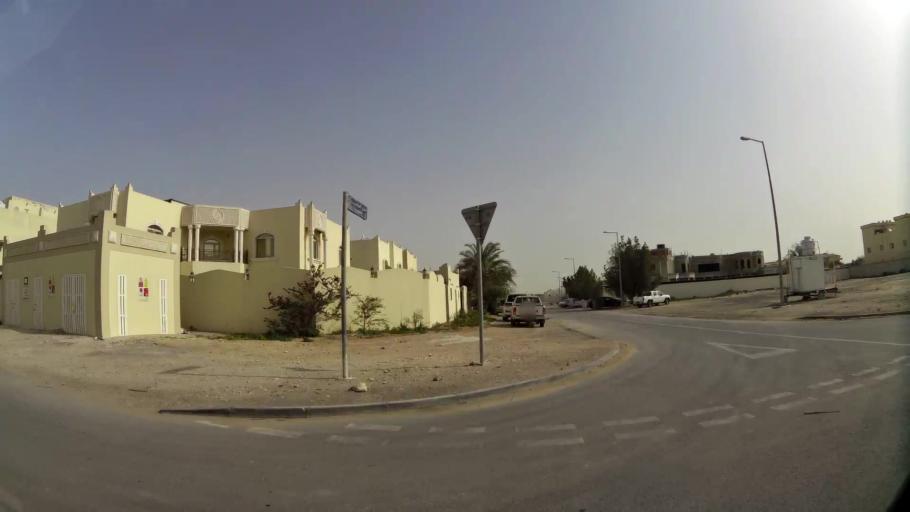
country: QA
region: Baladiyat ar Rayyan
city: Ar Rayyan
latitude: 25.2452
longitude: 51.4399
